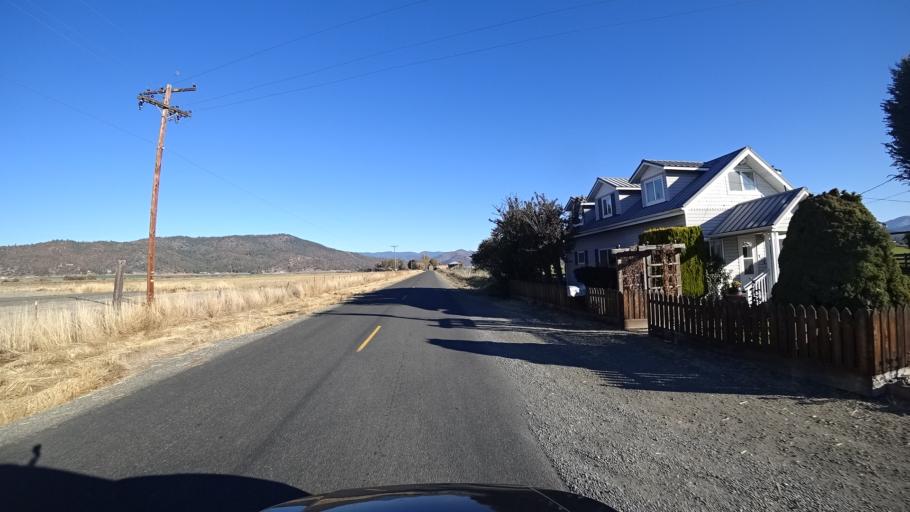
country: US
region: California
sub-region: Siskiyou County
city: Yreka
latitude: 41.5594
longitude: -122.8534
